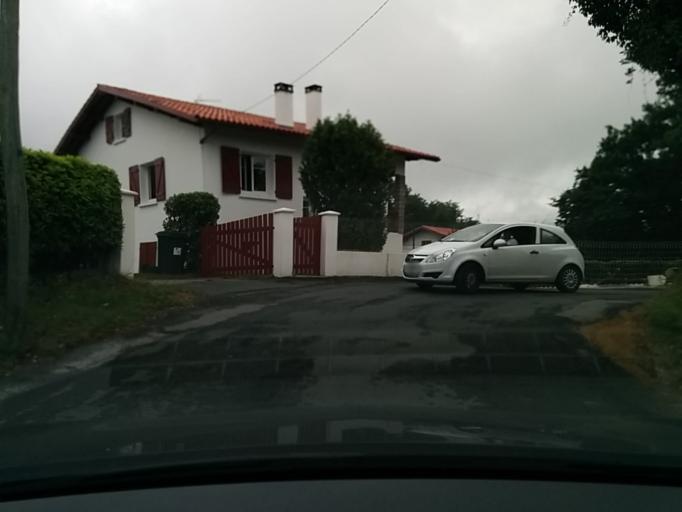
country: FR
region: Aquitaine
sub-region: Departement des Pyrenees-Atlantiques
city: Saint-Jean-de-Luz
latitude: 43.3927
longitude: -1.6355
